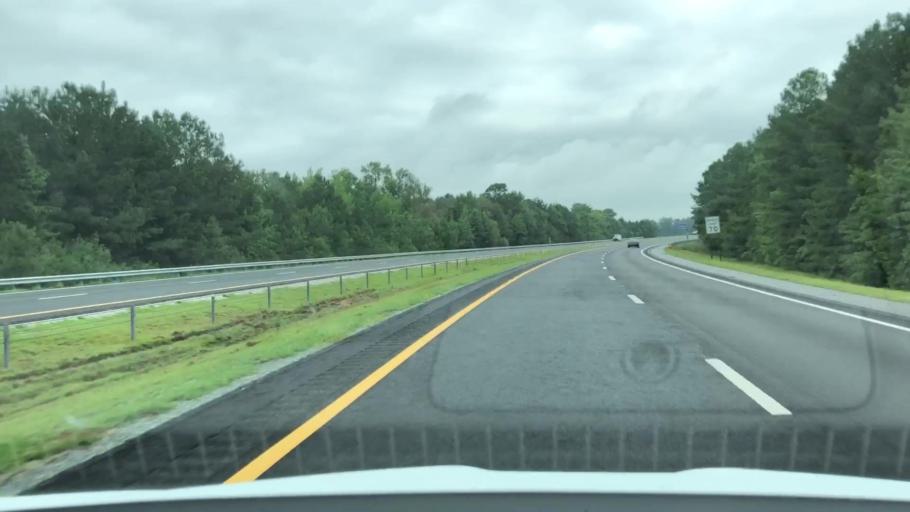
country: US
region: North Carolina
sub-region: Wayne County
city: Fremont
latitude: 35.5037
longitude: -77.9998
